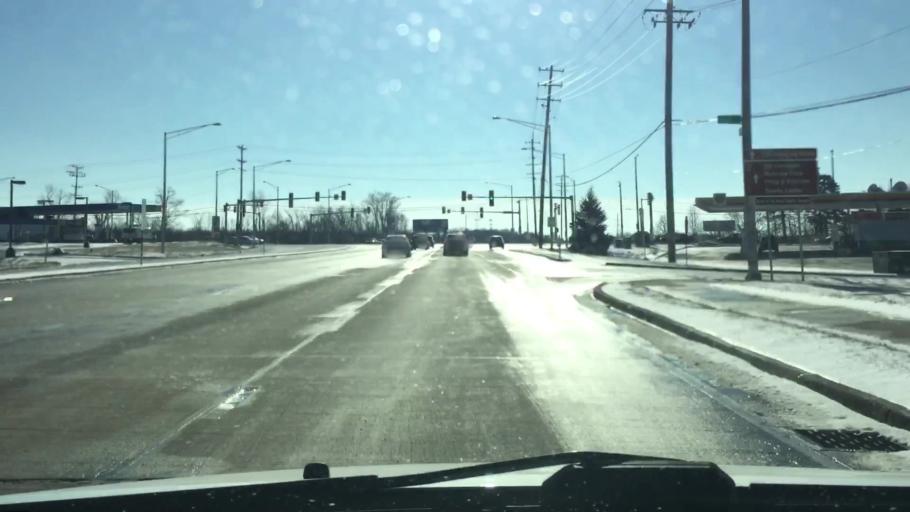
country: US
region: Illinois
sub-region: Kane County
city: Geneva
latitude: 41.8874
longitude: -88.2773
